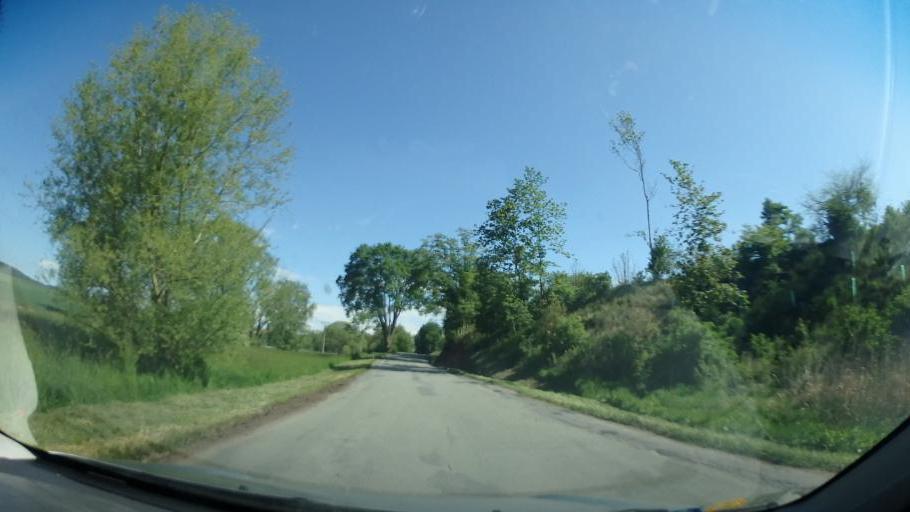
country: CZ
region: South Moravian
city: Velke Opatovice
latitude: 49.6692
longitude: 16.6322
